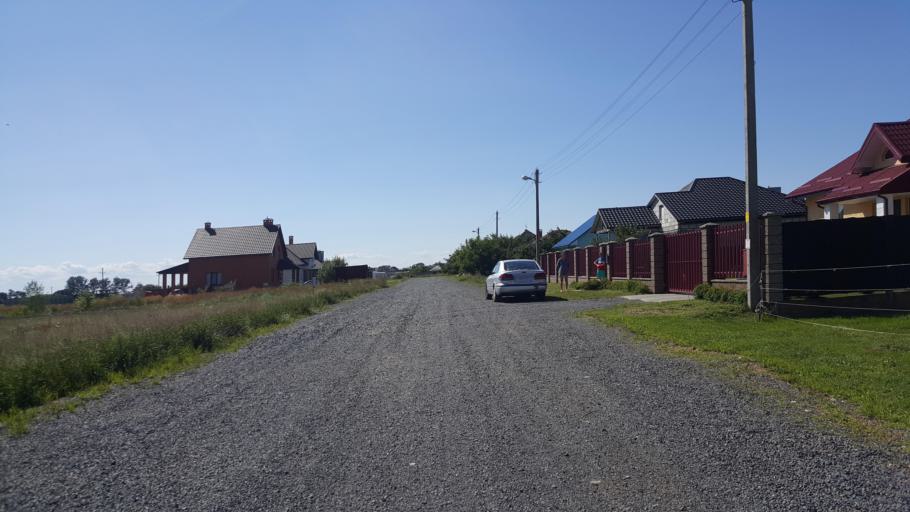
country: BY
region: Brest
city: Charnawchytsy
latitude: 52.2054
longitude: 23.7464
